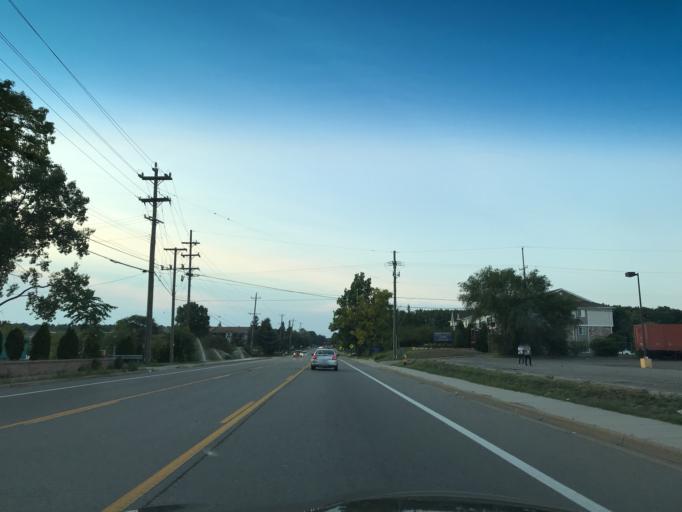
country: US
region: Michigan
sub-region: Washtenaw County
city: Ypsilanti
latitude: 42.2516
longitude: -83.6610
